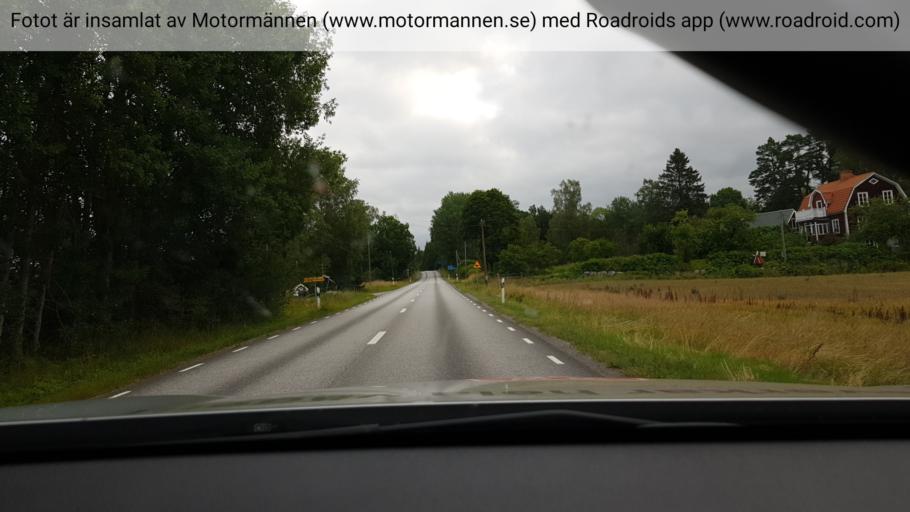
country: SE
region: Stockholm
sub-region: Norrtalje Kommun
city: Skanninge
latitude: 59.8559
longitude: 18.4471
